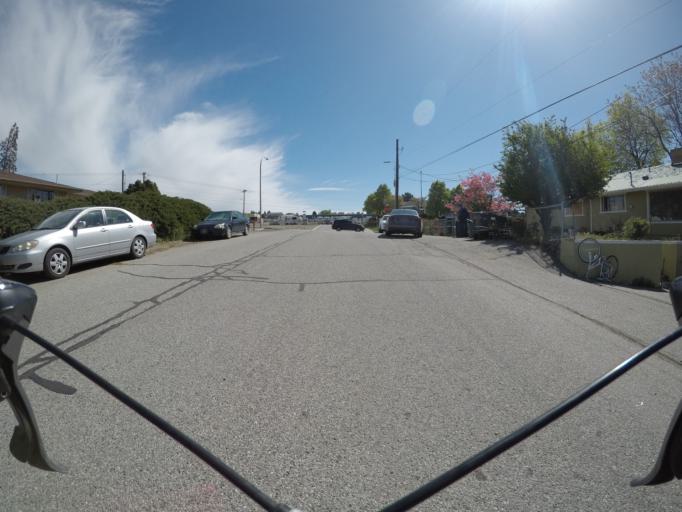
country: US
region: Washington
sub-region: Chelan County
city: South Wenatchee
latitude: 47.4037
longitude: -120.2824
